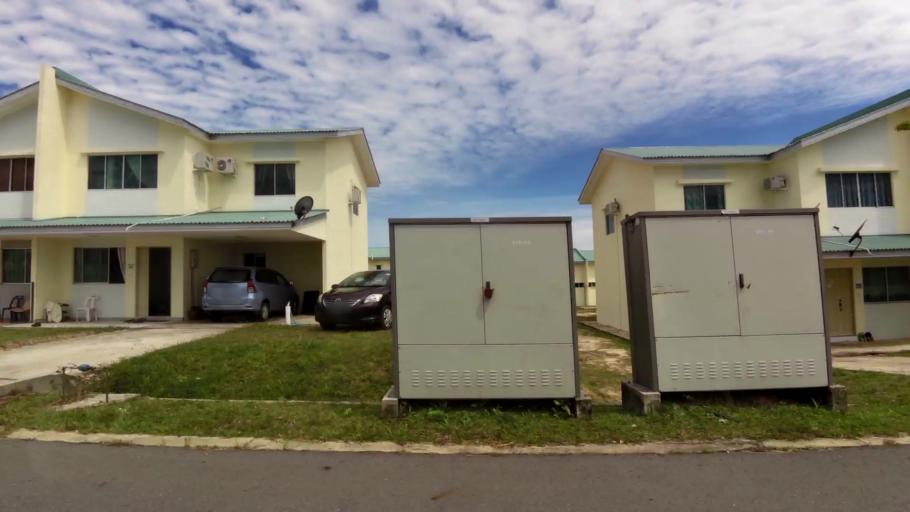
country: BN
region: Brunei and Muara
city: Bandar Seri Begawan
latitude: 4.9725
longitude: 115.0091
